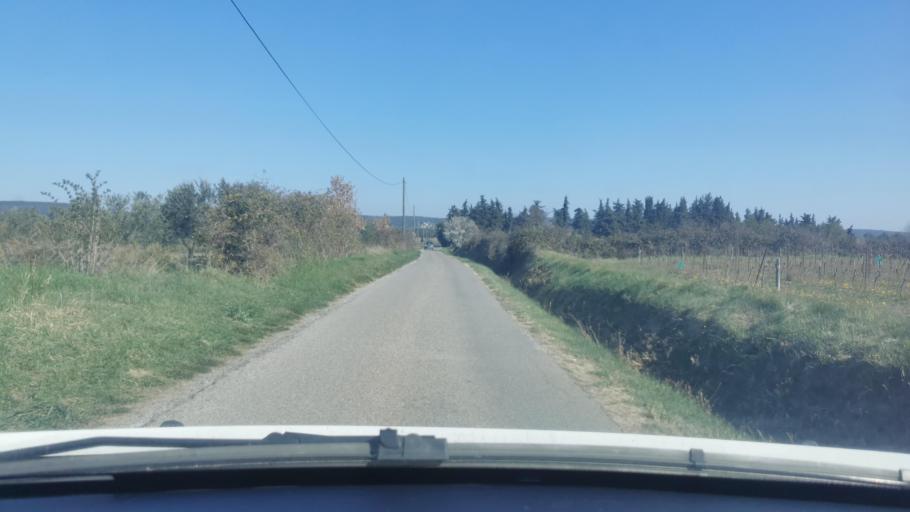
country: FR
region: Languedoc-Roussillon
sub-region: Departement du Gard
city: Montaren-et-Saint-Mediers
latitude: 44.0368
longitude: 4.3895
